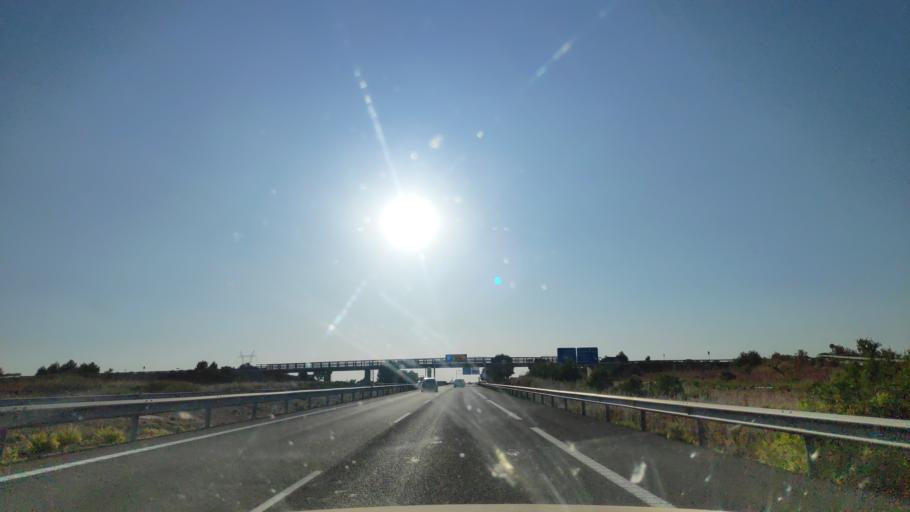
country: ES
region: Castille-La Mancha
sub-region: Provincia de Cuenca
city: Tarancon
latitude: 39.9945
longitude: -3.0066
